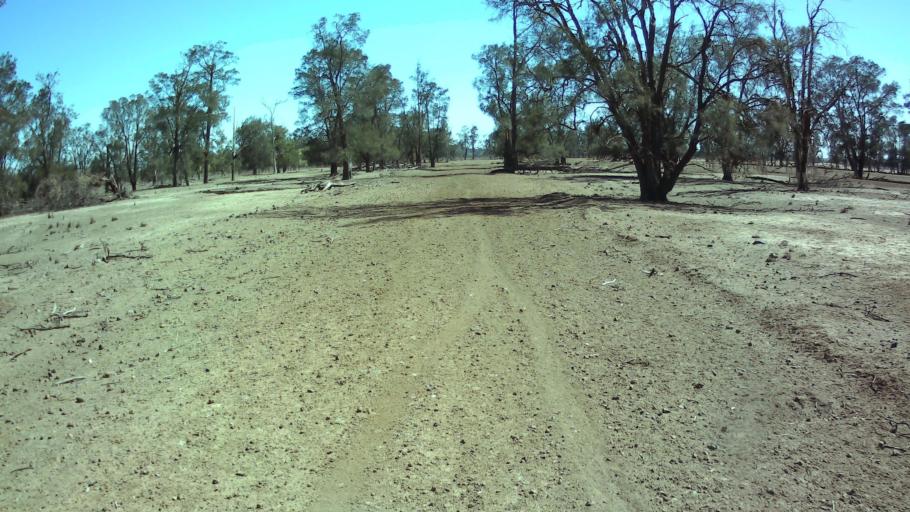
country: AU
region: New South Wales
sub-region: Bland
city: West Wyalong
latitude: -33.7605
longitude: 147.6586
